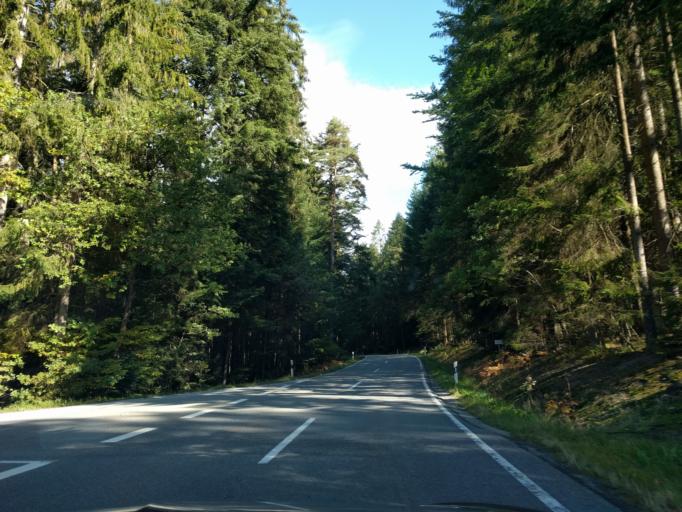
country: DE
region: Bavaria
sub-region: Lower Bavaria
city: Viechtach
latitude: 49.1258
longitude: 12.8882
